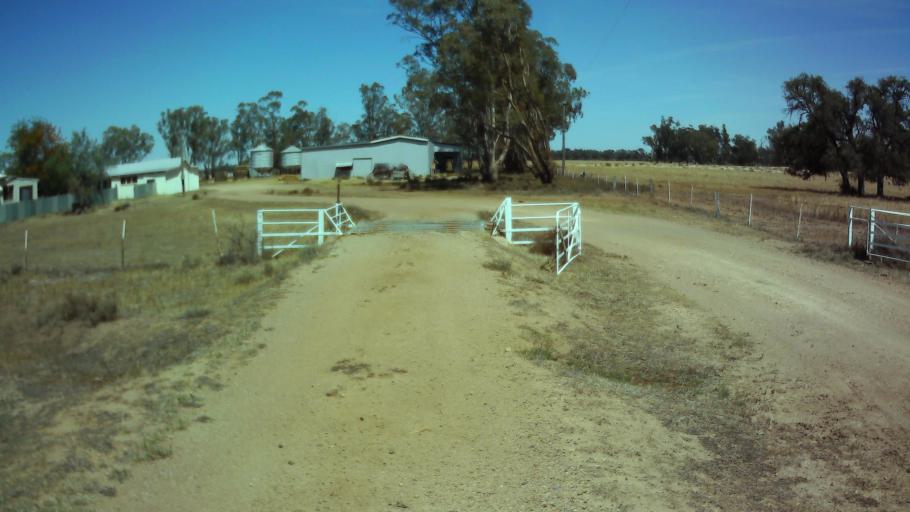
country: AU
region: New South Wales
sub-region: Weddin
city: Grenfell
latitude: -34.0479
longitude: 147.9174
